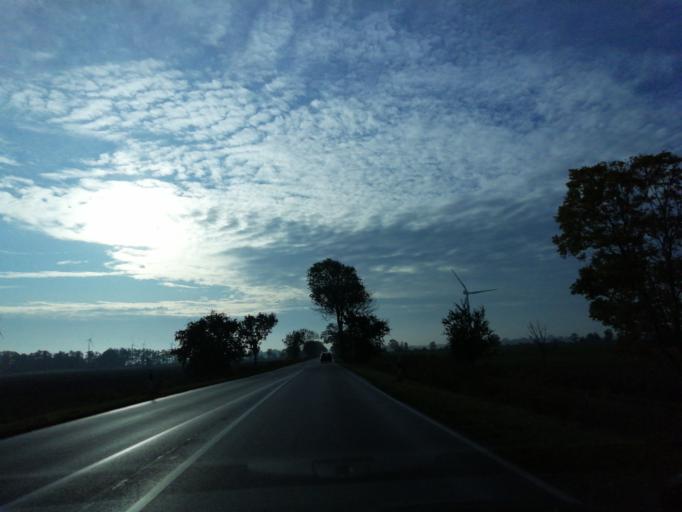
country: DE
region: Lower Saxony
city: Fedderwarden
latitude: 53.6145
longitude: 8.0393
